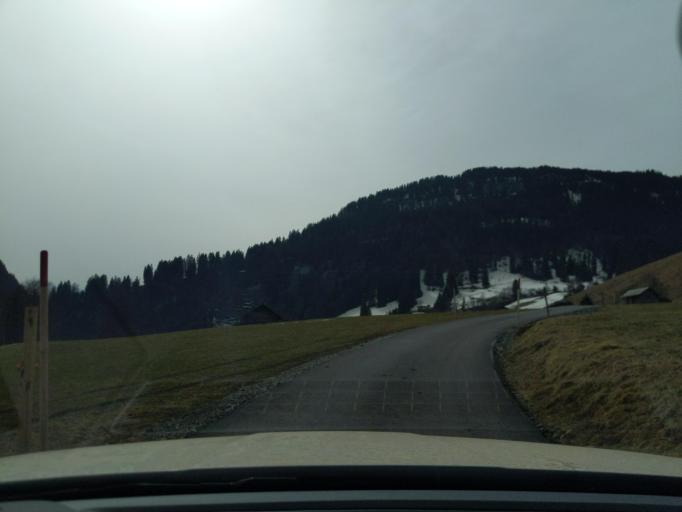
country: DE
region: Bavaria
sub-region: Swabia
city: Obermaiselstein
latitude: 47.4438
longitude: 10.2358
